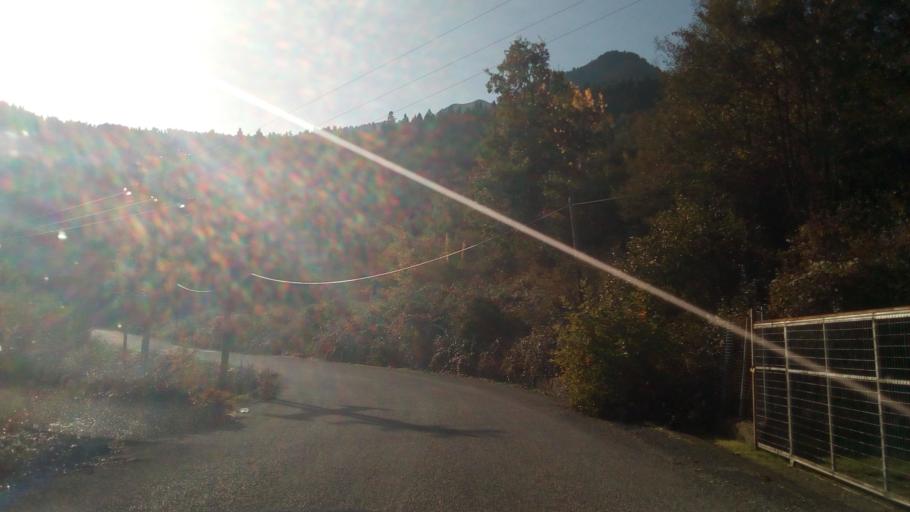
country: GR
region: West Greece
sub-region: Nomos Aitolias kai Akarnanias
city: Thermo
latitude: 38.6558
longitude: 21.8465
